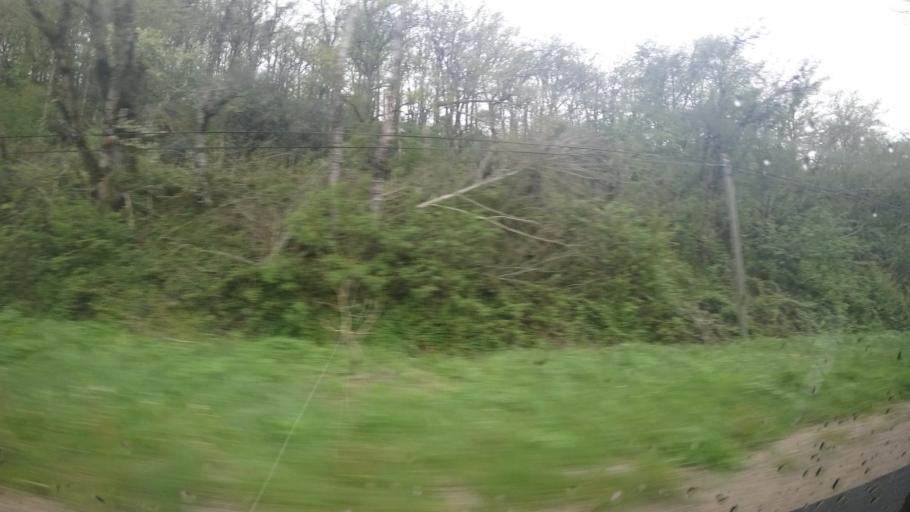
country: FR
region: Midi-Pyrenees
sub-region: Departement de l'Aveyron
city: Laissac
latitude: 44.2738
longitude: 2.8621
